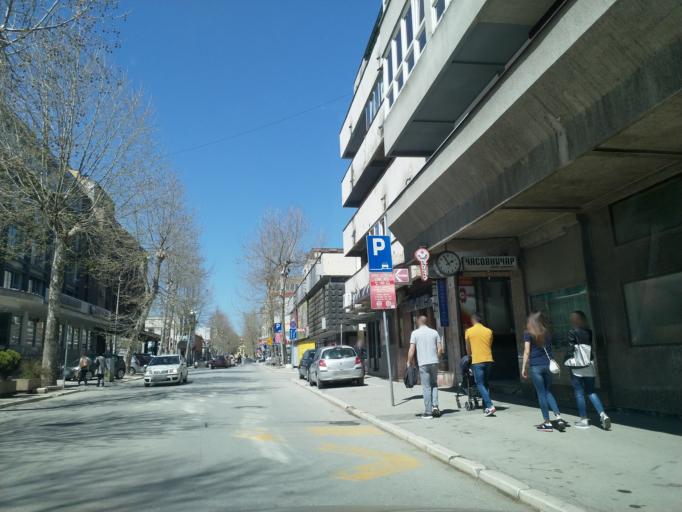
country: RS
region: Central Serbia
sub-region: Kolubarski Okrug
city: Valjevo
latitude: 44.2700
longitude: 19.8864
